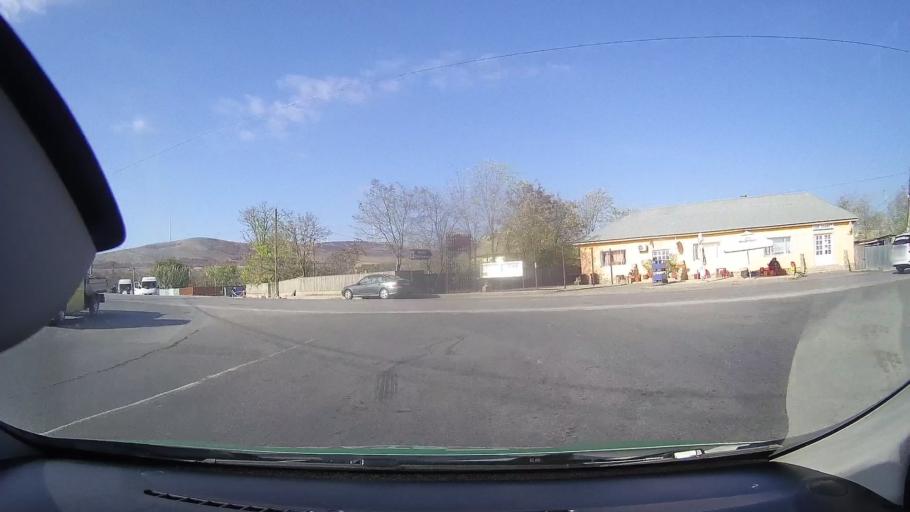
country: RO
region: Tulcea
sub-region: Comuna Valea Nucarilor
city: Agighiol
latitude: 45.0331
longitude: 28.8801
